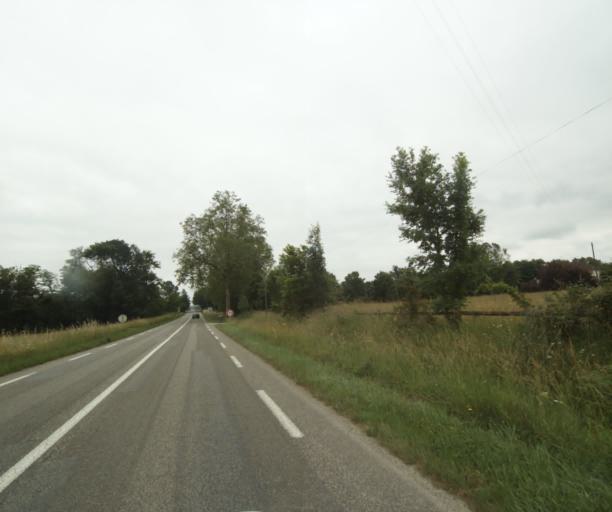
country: FR
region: Midi-Pyrenees
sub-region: Departement du Tarn-et-Garonne
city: Saint-Nauphary
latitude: 43.9719
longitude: 1.4195
